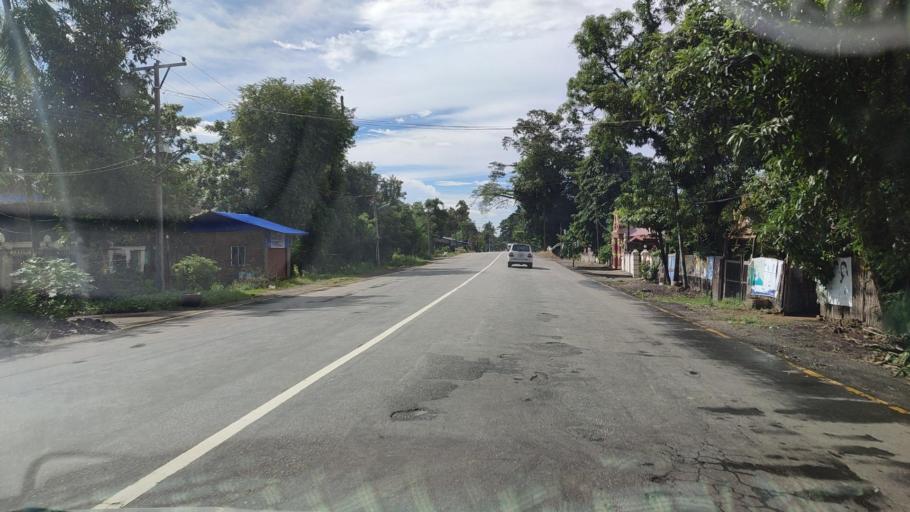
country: MM
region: Bago
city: Pyu
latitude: 18.3305
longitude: 96.4960
